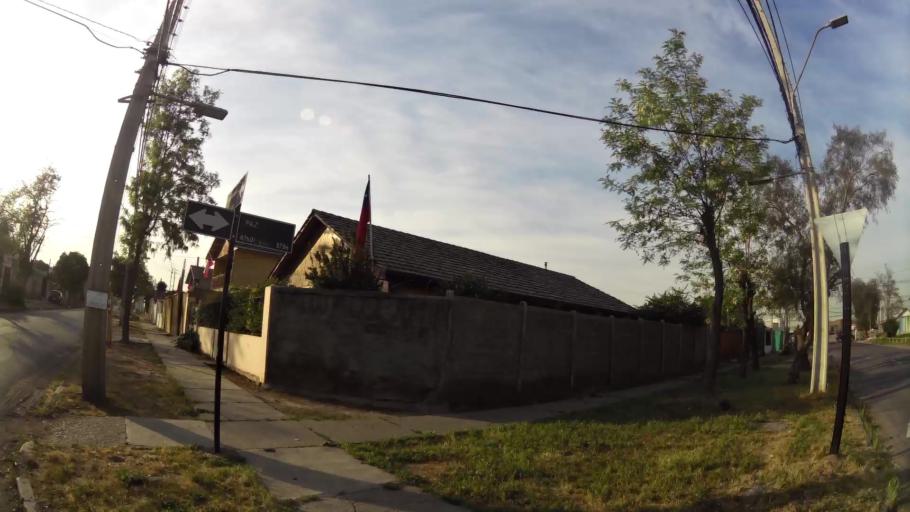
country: CL
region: Santiago Metropolitan
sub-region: Provincia de Santiago
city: La Pintana
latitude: -33.5337
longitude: -70.6727
